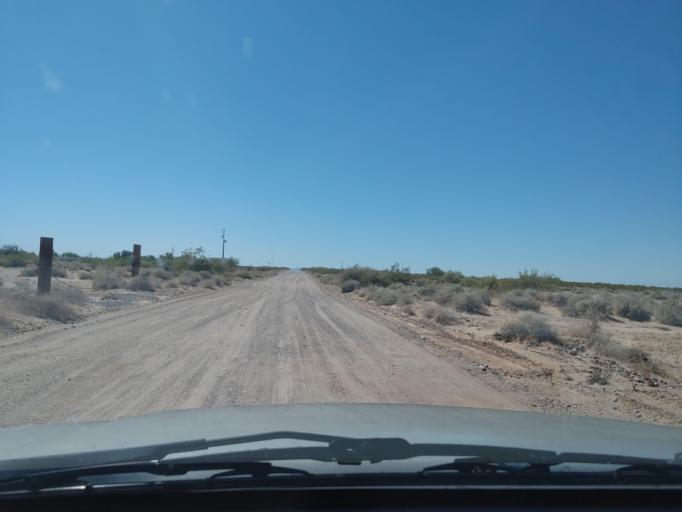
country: US
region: Arizona
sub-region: Maricopa County
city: Gila Bend
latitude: 32.9900
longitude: -113.3404
